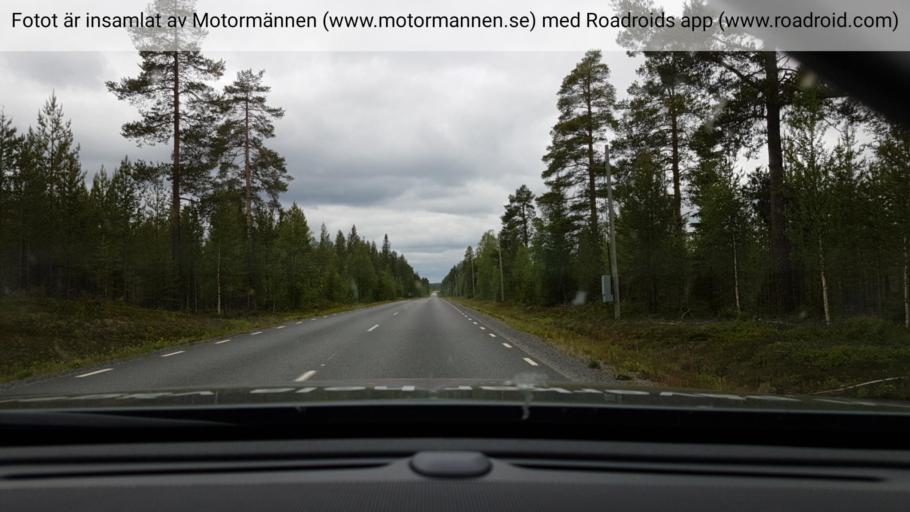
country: SE
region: Vaesterbotten
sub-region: Sorsele Kommun
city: Sorsele
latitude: 65.6639
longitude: 17.4067
